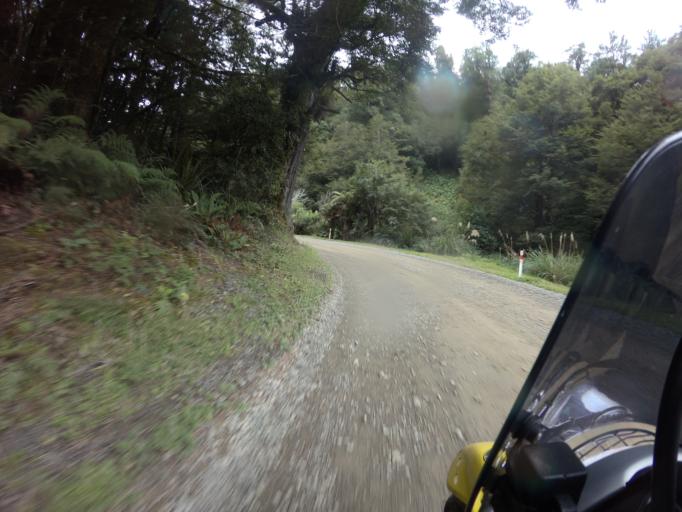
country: NZ
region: Bay of Plenty
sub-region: Whakatane District
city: Murupara
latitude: -38.6755
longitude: 177.0522
